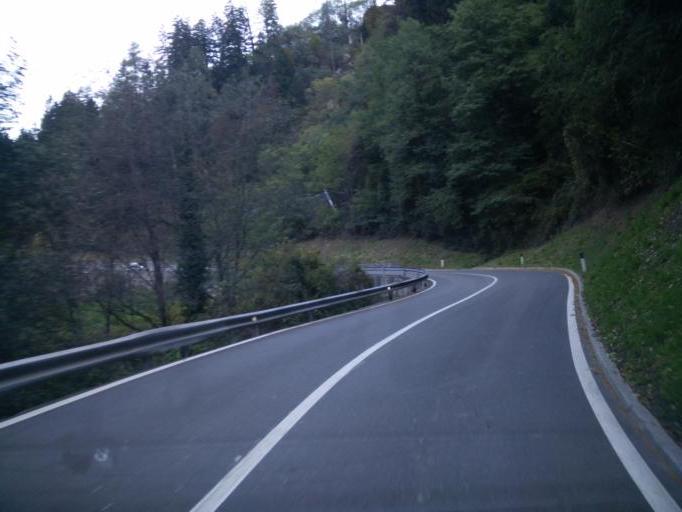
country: IT
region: Trentino-Alto Adige
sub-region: Bolzano
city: San Leonardo in Passiria
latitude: 46.8176
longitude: 11.2383
